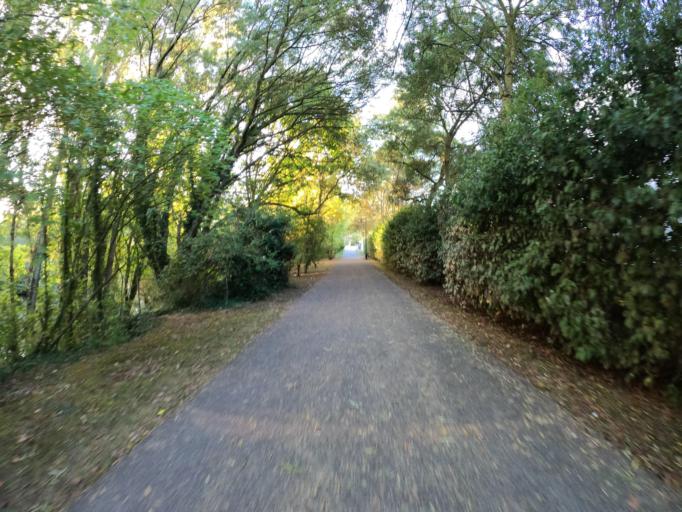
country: ES
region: Navarre
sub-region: Provincia de Navarra
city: Baranain
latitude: 42.8096
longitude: -1.6815
